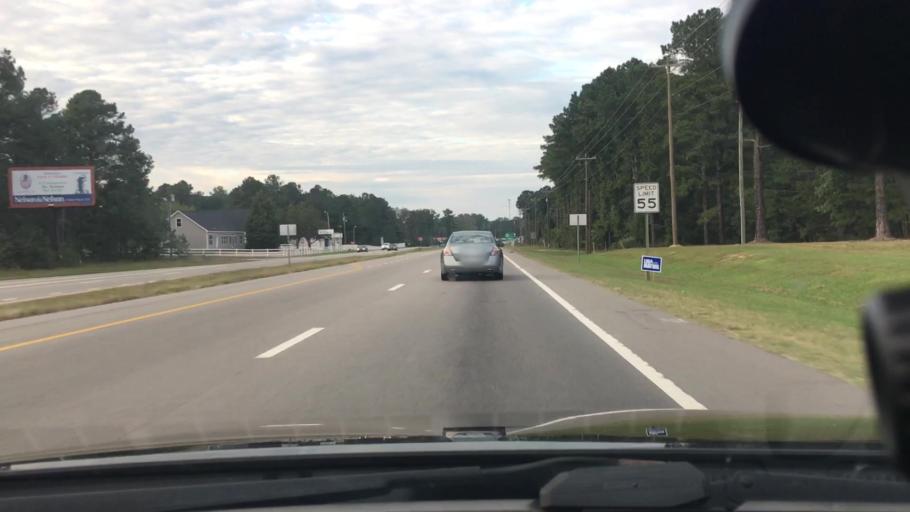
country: US
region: North Carolina
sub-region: Lee County
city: Sanford
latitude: 35.4051
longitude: -79.2314
